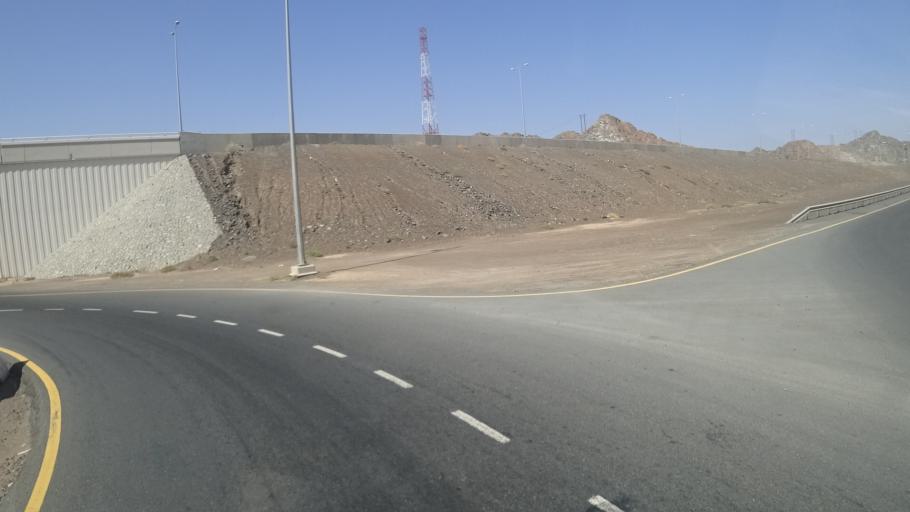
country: OM
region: Ash Sharqiyah
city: Ibra'
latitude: 22.6864
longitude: 58.5818
